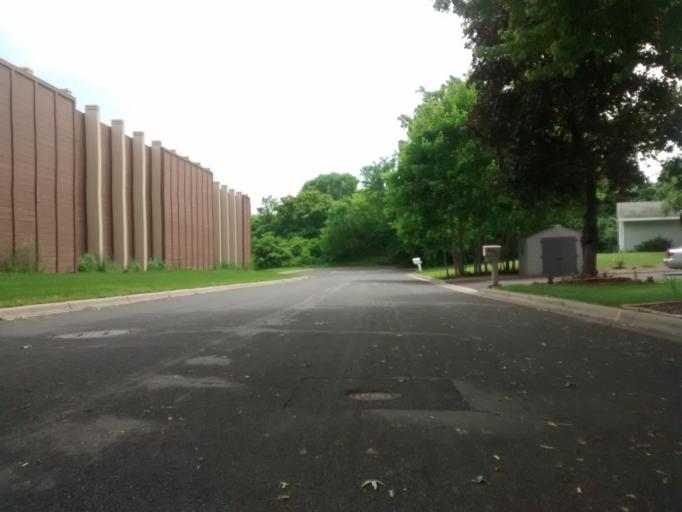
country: US
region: Minnesota
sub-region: Dakota County
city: Burnsville
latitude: 44.7531
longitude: -93.2873
